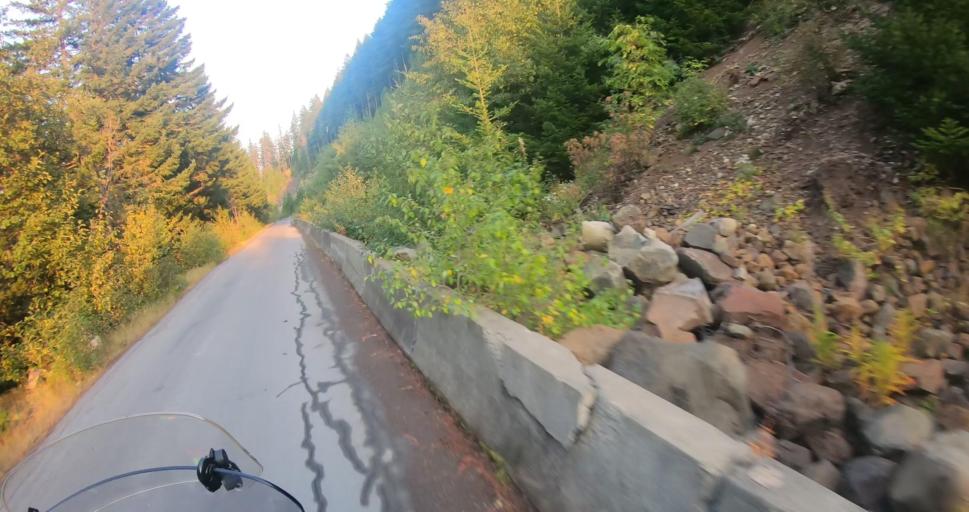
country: US
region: Oregon
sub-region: Hood River County
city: Odell
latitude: 45.4619
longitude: -121.6421
